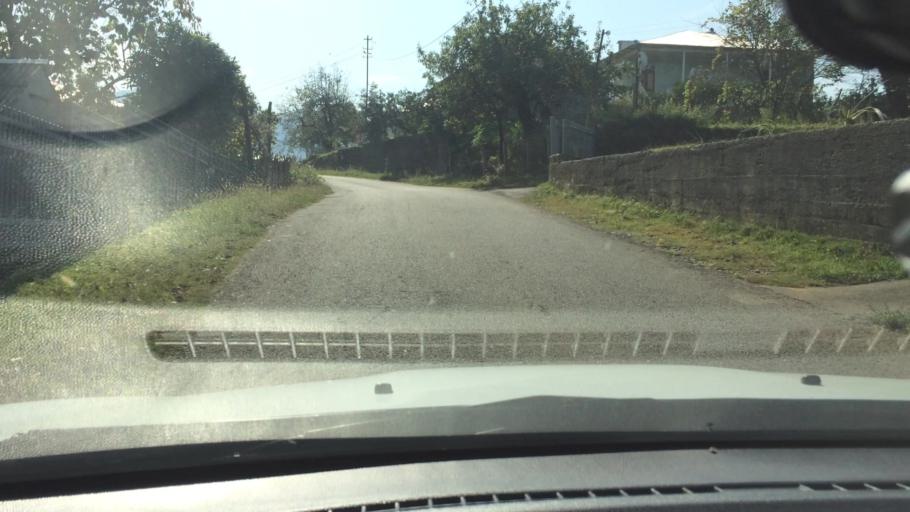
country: GE
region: Ajaria
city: Kobuleti
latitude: 41.8143
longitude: 41.8234
